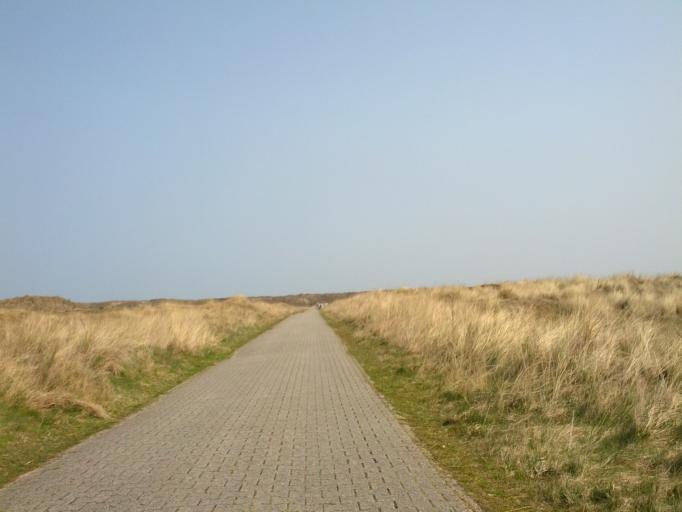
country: DE
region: Lower Saxony
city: Langeoog
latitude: 53.7499
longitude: 7.5127
